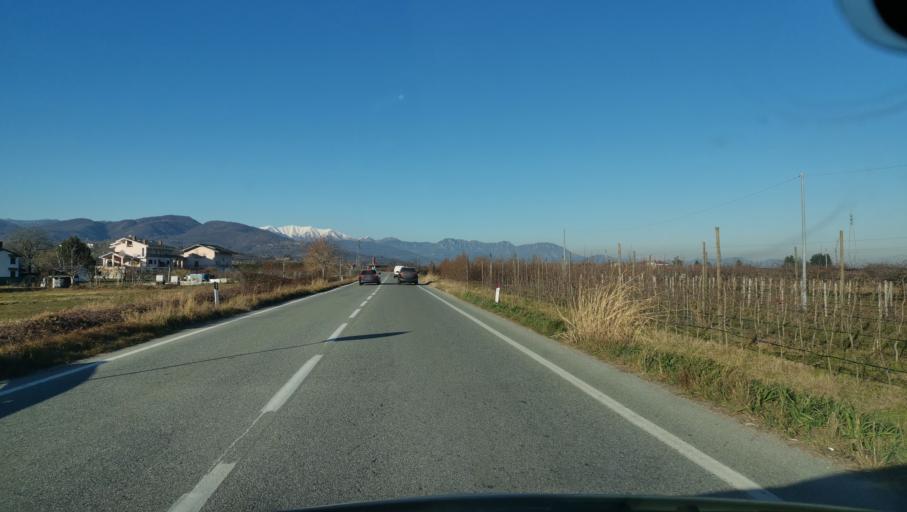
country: IT
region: Piedmont
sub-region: Provincia di Torino
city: Bibiana
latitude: 44.7981
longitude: 7.2964
